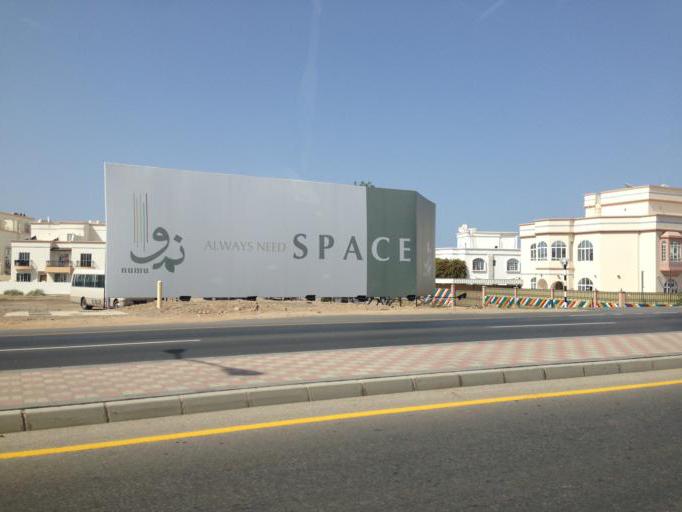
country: OM
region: Muhafazat Masqat
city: Bawshar
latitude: 23.5992
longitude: 58.3825
